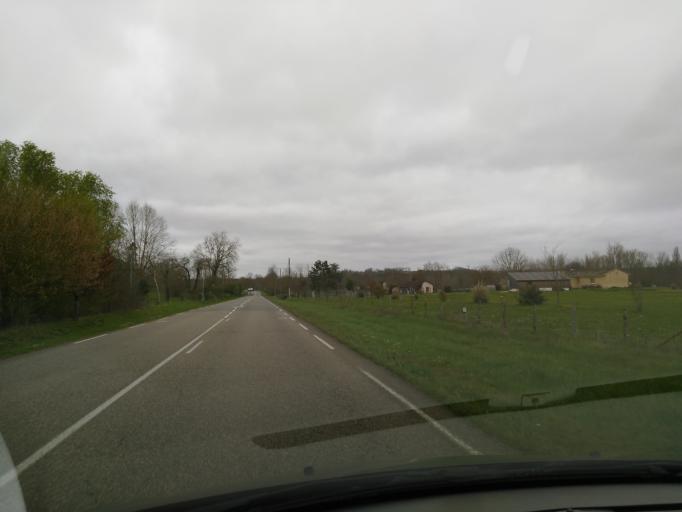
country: FR
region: Aquitaine
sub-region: Departement du Lot-et-Garonne
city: Castillonnes
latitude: 44.6664
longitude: 0.5834
